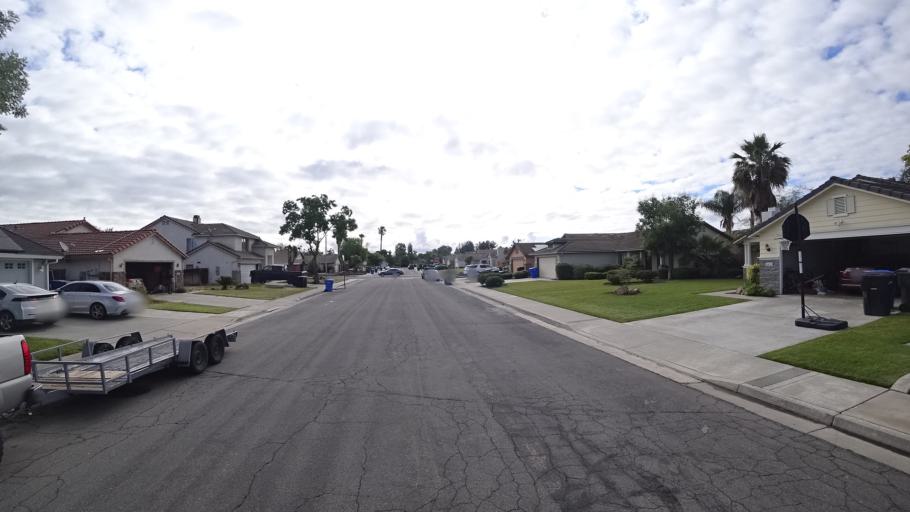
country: US
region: California
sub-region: Kings County
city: Hanford
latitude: 36.3602
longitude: -119.6340
